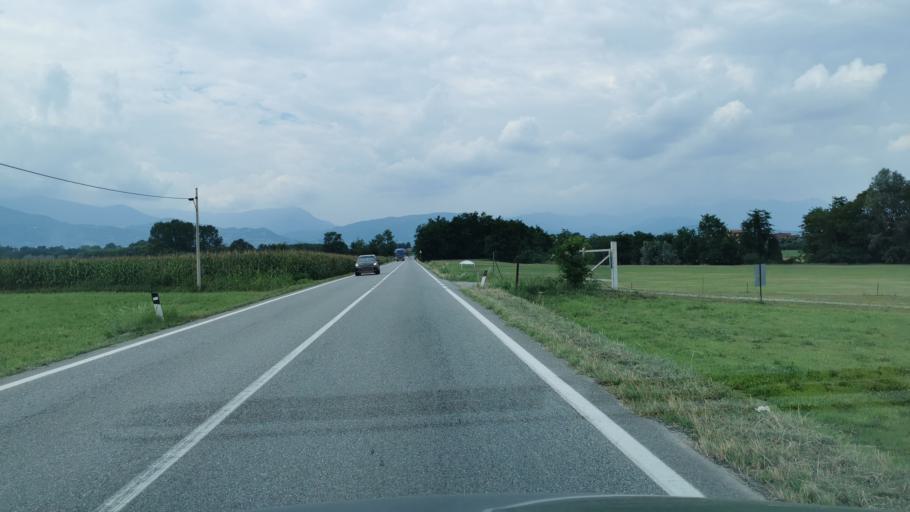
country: IT
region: Piedmont
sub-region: Provincia di Torino
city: Garzigliana
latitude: 44.8333
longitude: 7.3634
